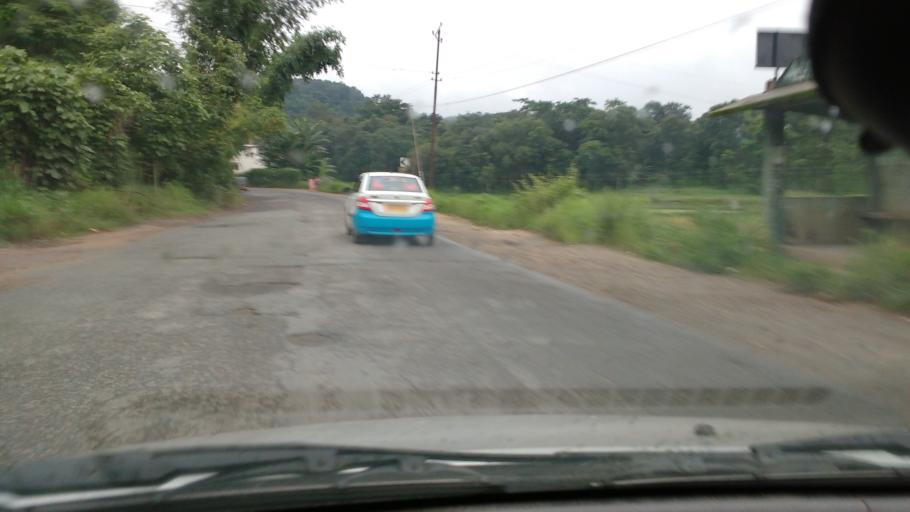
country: IN
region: Meghalaya
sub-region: Ri-Bhoi
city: Nongpoh
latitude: 25.7399
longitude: 91.8871
